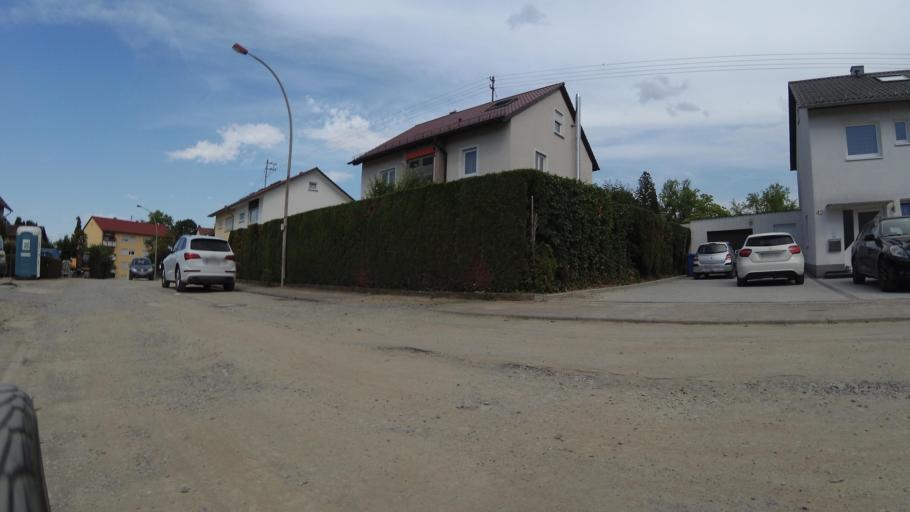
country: DE
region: Baden-Wuerttemberg
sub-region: Regierungsbezirk Stuttgart
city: Bad Rappenau
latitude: 49.2424
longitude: 9.1118
